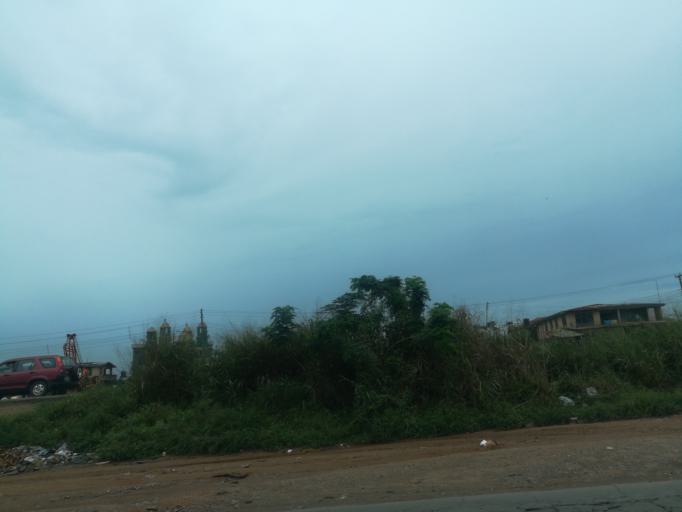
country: NG
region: Oyo
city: Ibadan
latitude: 7.3391
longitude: 3.9049
